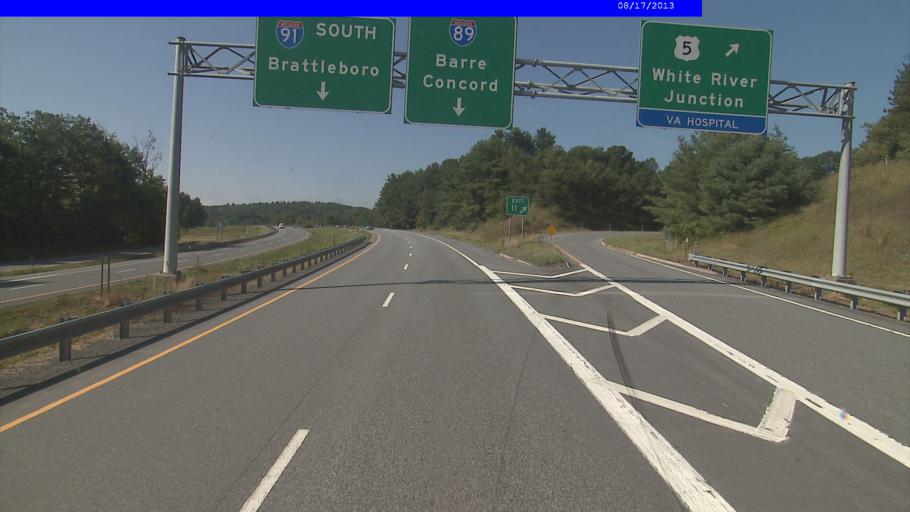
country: US
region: Vermont
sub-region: Windsor County
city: White River Junction
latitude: 43.6483
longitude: -72.3365
